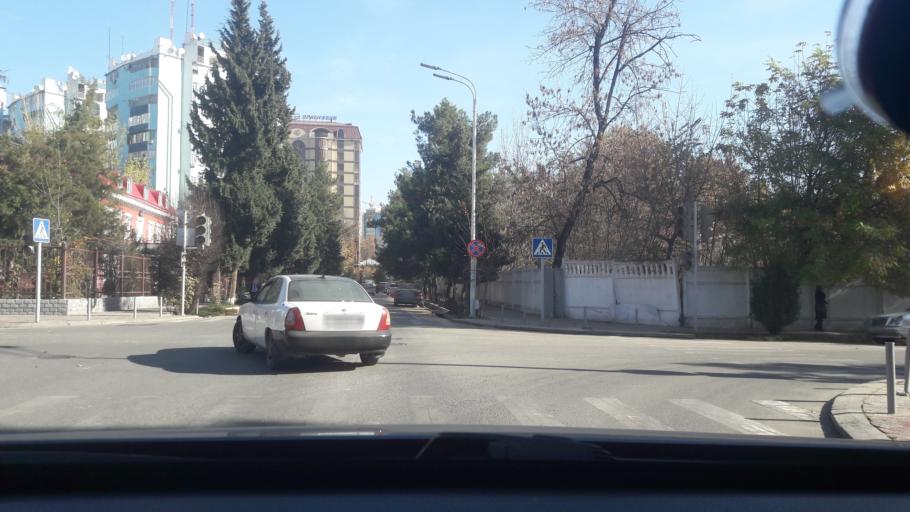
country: TJ
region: Dushanbe
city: Dushanbe
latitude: 38.5745
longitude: 68.7892
